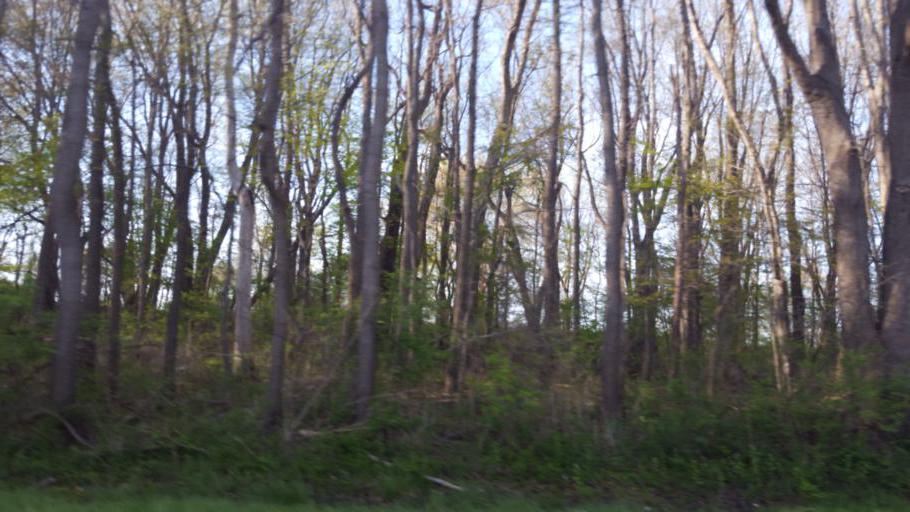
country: US
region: Ohio
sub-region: Ashtabula County
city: North Kingsville
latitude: 41.9164
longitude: -80.7389
